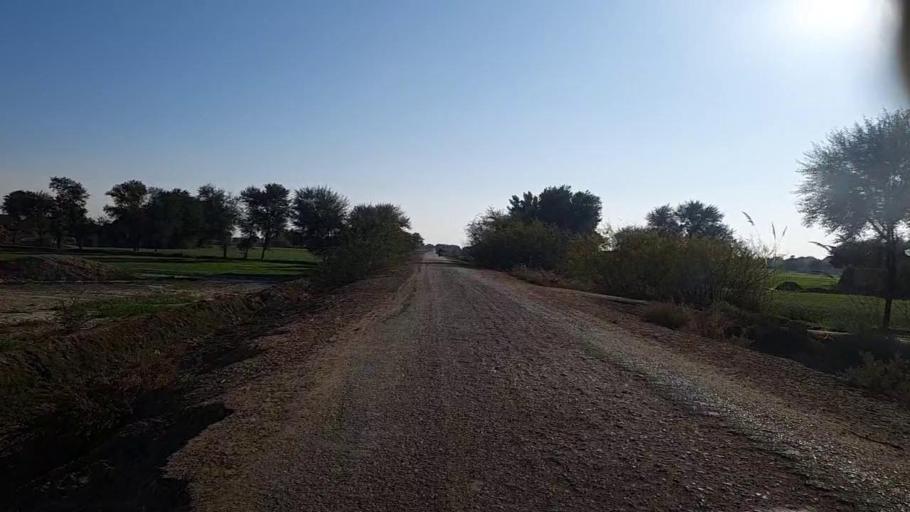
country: PK
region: Sindh
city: Khairpur
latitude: 27.8947
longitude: 69.7467
